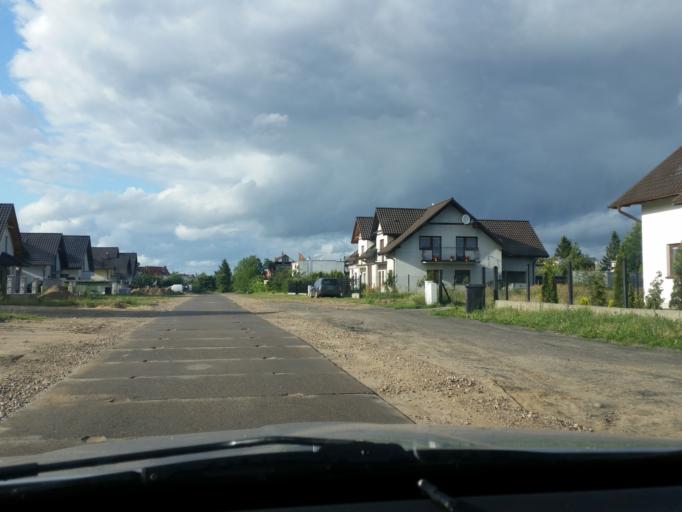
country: PL
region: Pomeranian Voivodeship
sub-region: Powiat chojnicki
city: Chojnice
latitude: 53.7019
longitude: 17.5443
